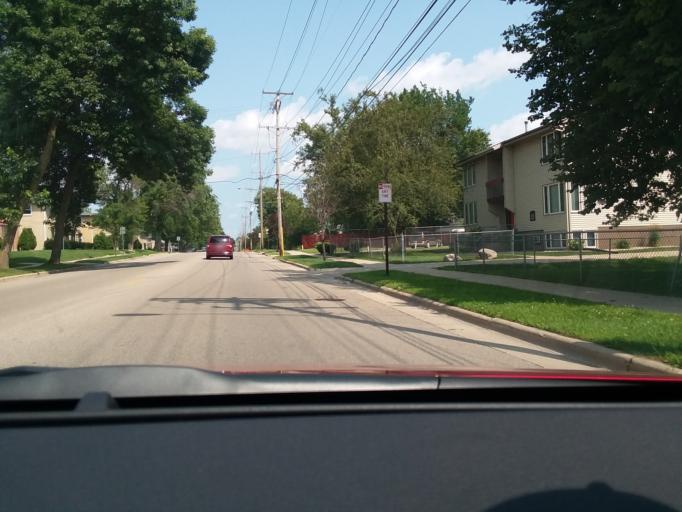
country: US
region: Wisconsin
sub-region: Dane County
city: Madison
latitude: 43.0386
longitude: -89.4012
